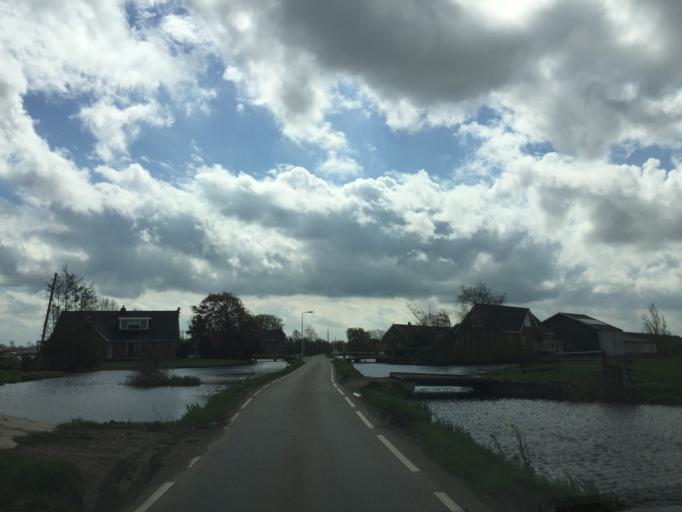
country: NL
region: South Holland
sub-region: Gemeente Gouda
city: Bloemendaal
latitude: 52.0537
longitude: 4.6966
